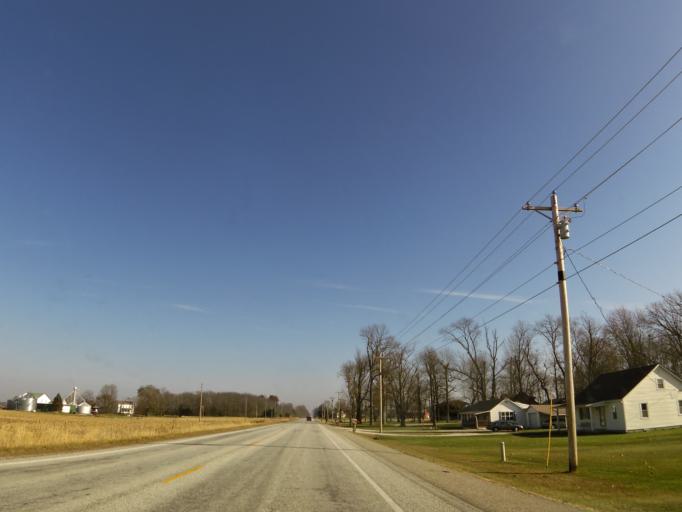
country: US
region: Indiana
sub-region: Shelby County
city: Shelbyville
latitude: 39.5423
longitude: -85.6987
